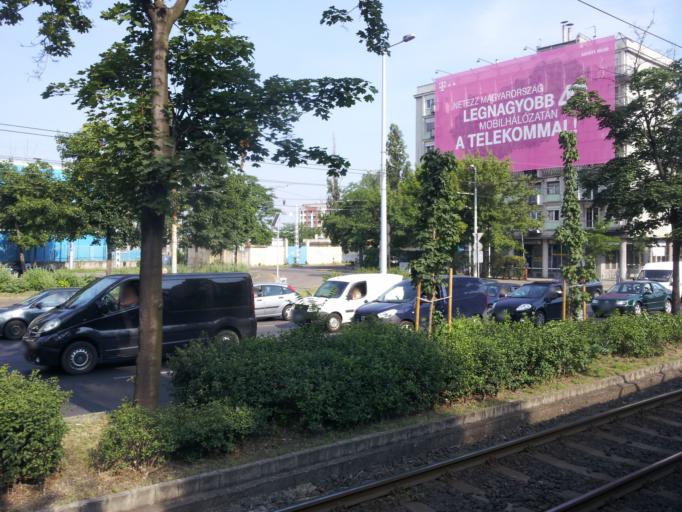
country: HU
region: Budapest
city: Budapest XIV. keruelet
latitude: 47.4914
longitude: 19.1088
